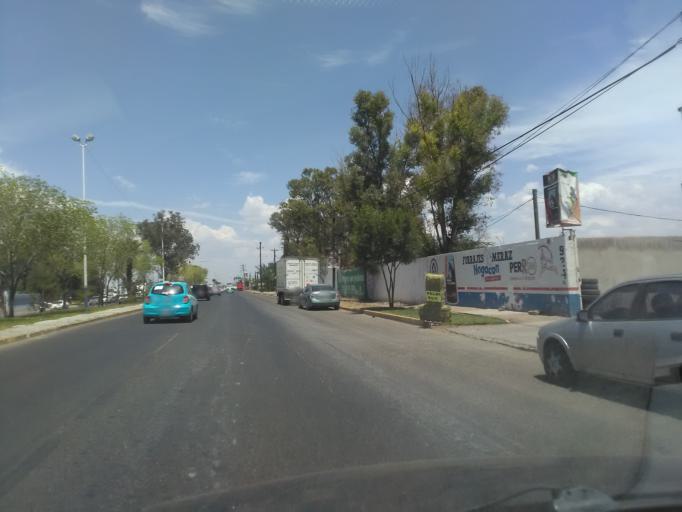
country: MX
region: Durango
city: Victoria de Durango
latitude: 24.0307
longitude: -104.6164
